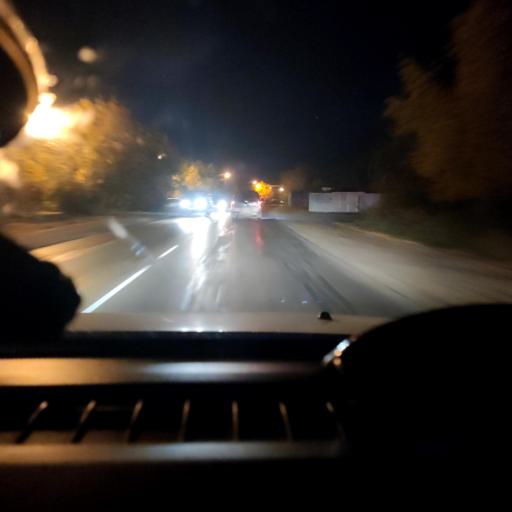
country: RU
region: Samara
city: Rozhdestveno
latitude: 53.1452
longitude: 50.0675
